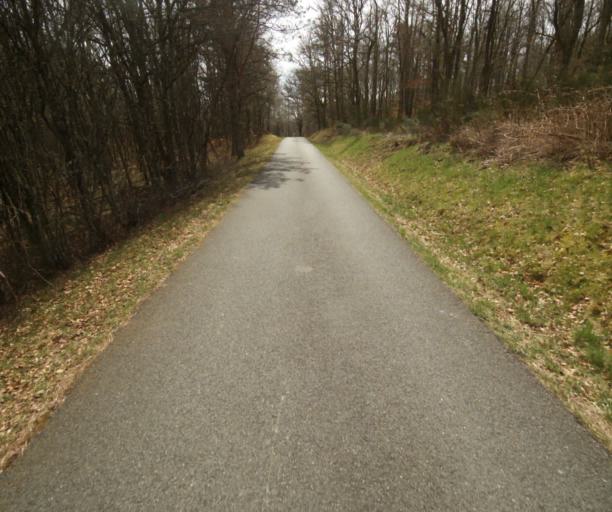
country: FR
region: Limousin
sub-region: Departement de la Correze
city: Egletons
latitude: 45.3720
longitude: 1.9672
